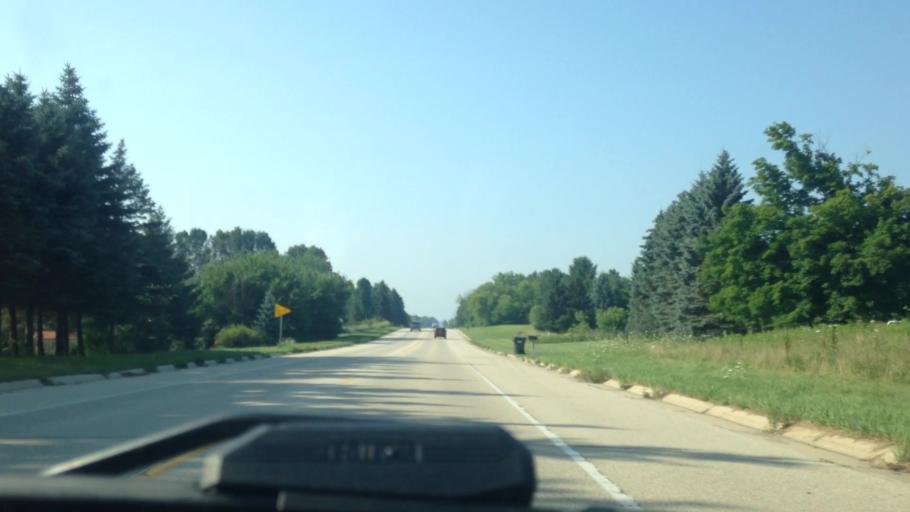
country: US
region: Wisconsin
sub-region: Washington County
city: Slinger
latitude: 43.3213
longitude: -88.2607
